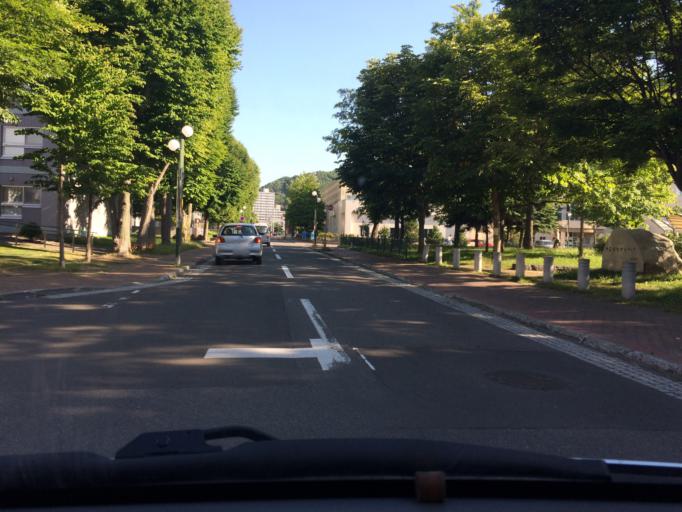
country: JP
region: Hokkaido
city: Sapporo
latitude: 43.0298
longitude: 141.3415
